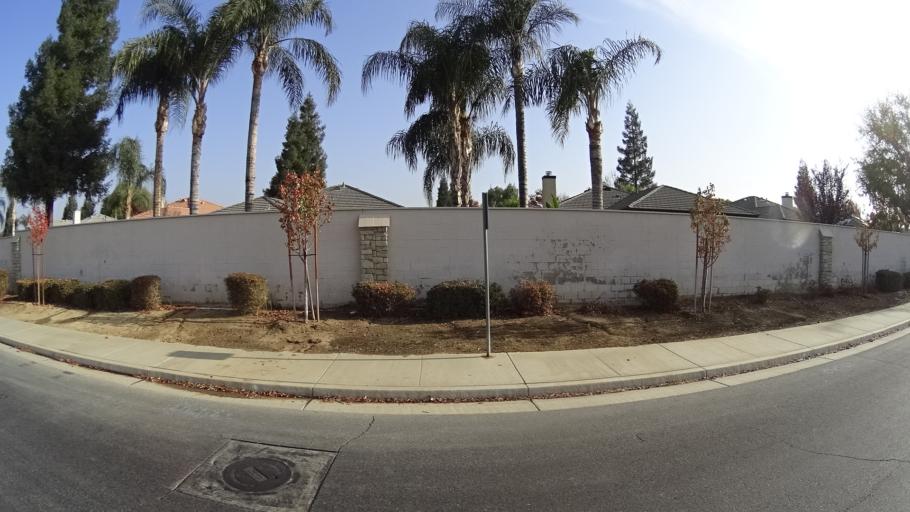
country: US
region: California
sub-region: Kern County
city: Greenacres
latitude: 35.4213
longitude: -119.1163
